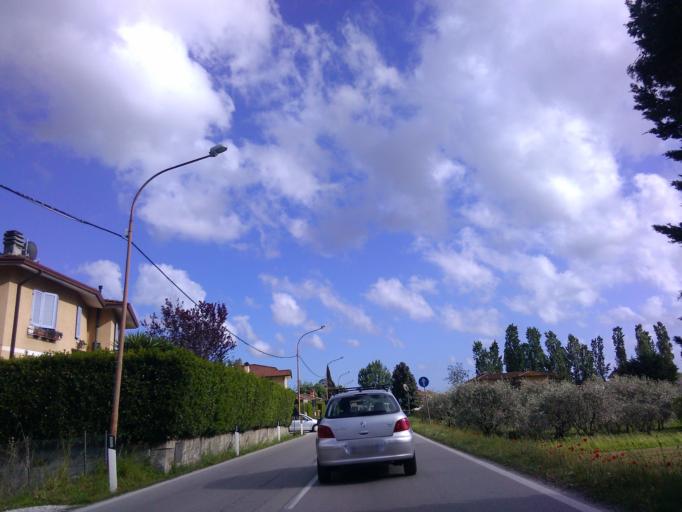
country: IT
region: Tuscany
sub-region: Provincia di Lucca
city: Ripa-Pozzi-Querceta-Ponterosso
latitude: 43.9673
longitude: 10.2212
